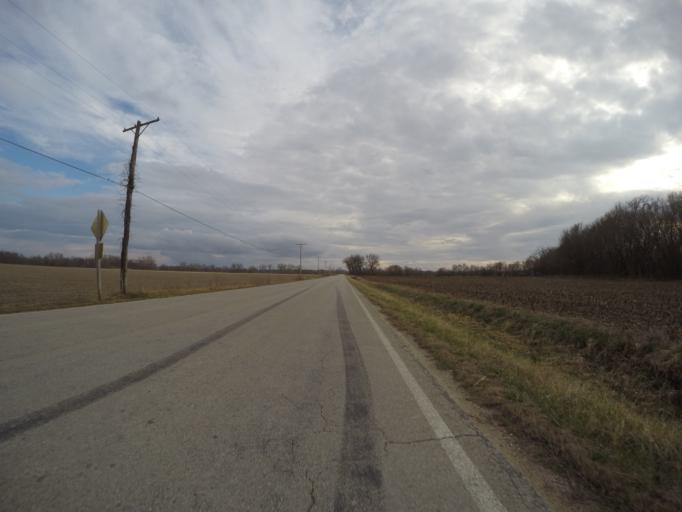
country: US
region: Kansas
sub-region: Riley County
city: Manhattan
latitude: 39.2458
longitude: -96.5705
